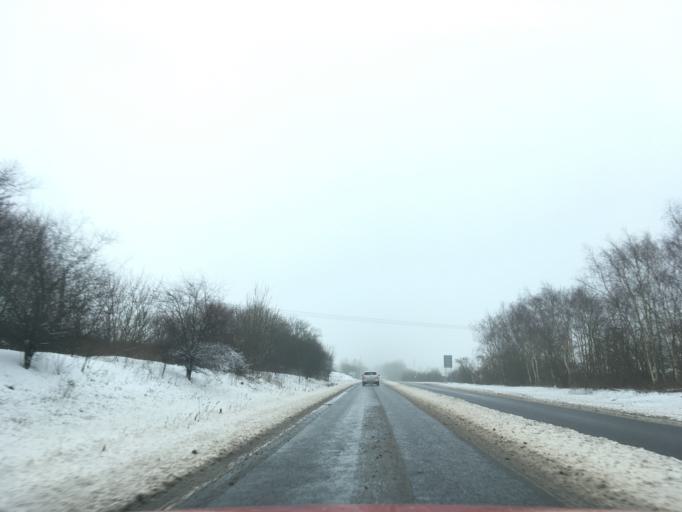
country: GB
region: England
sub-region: Warwickshire
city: Alcester
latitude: 52.2081
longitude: -1.8308
